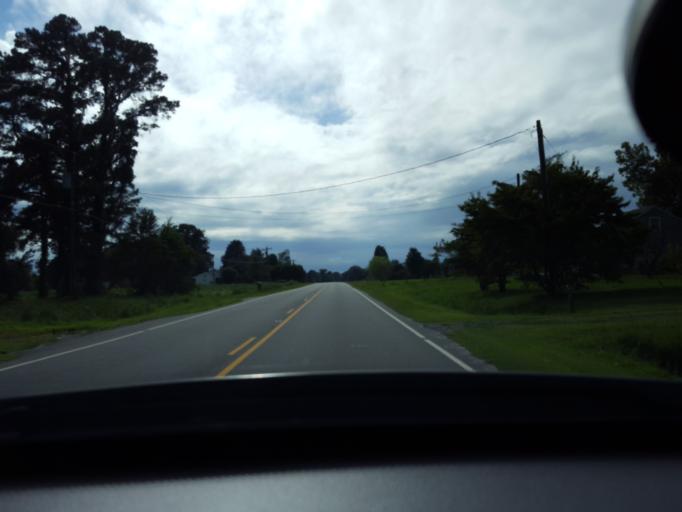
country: US
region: North Carolina
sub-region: Duplin County
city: Kenansville
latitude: 35.0133
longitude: -77.8791
